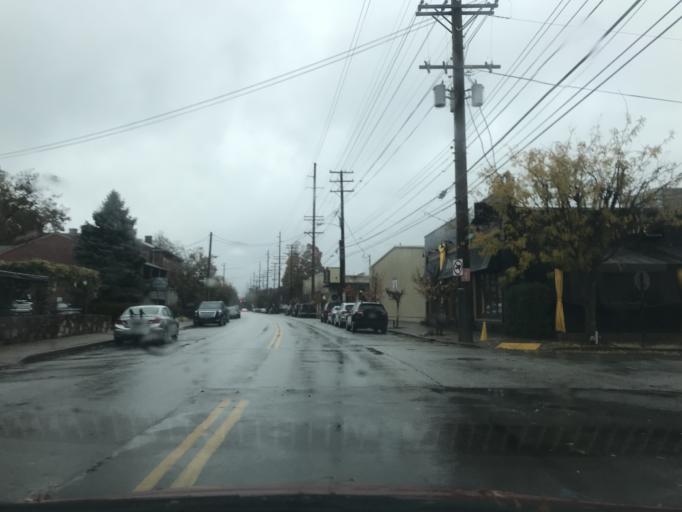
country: US
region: Indiana
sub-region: Clark County
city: Jeffersonville
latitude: 38.2534
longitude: -85.7032
